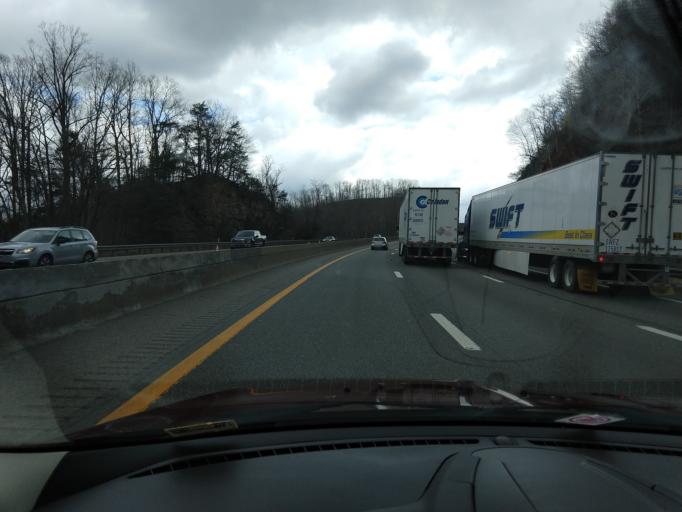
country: US
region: West Virginia
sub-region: Fayette County
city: Oak Hill
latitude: 37.9902
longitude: -81.3238
